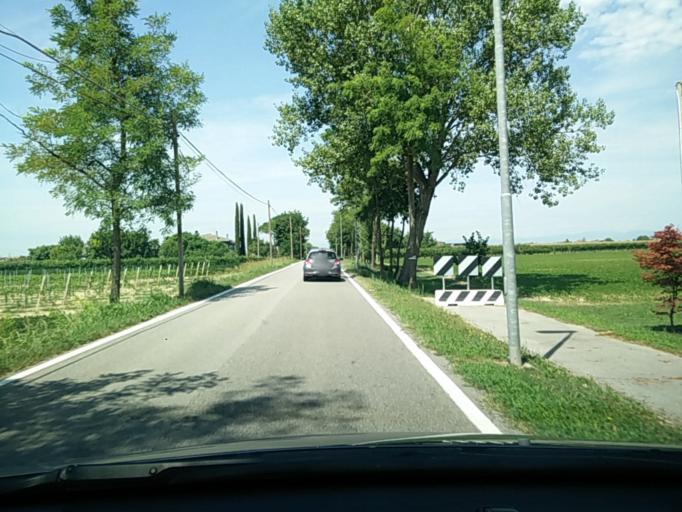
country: IT
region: Veneto
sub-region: Provincia di Venezia
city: Passarella
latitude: 45.5729
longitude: 12.6183
